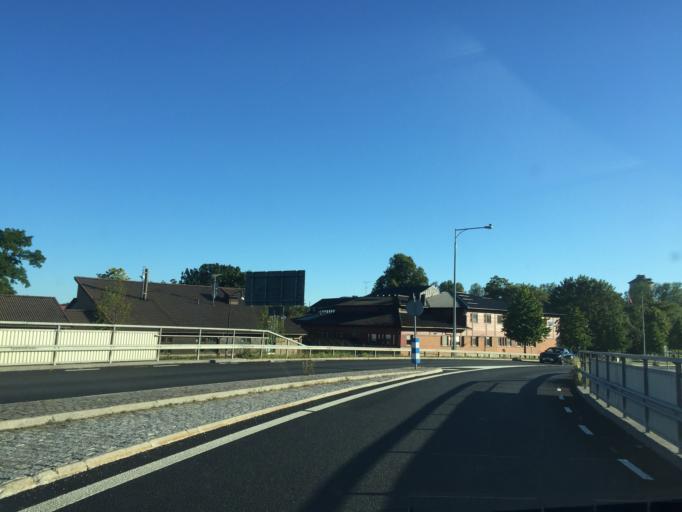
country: SE
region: OErebro
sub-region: Orebro Kommun
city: Orebro
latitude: 59.2653
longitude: 15.2001
